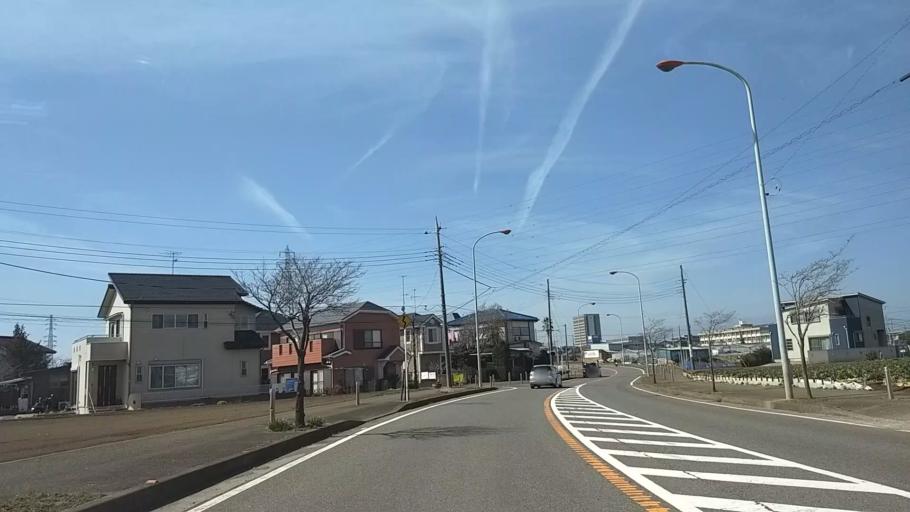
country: JP
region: Kanagawa
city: Fujisawa
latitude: 35.3794
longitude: 139.4820
